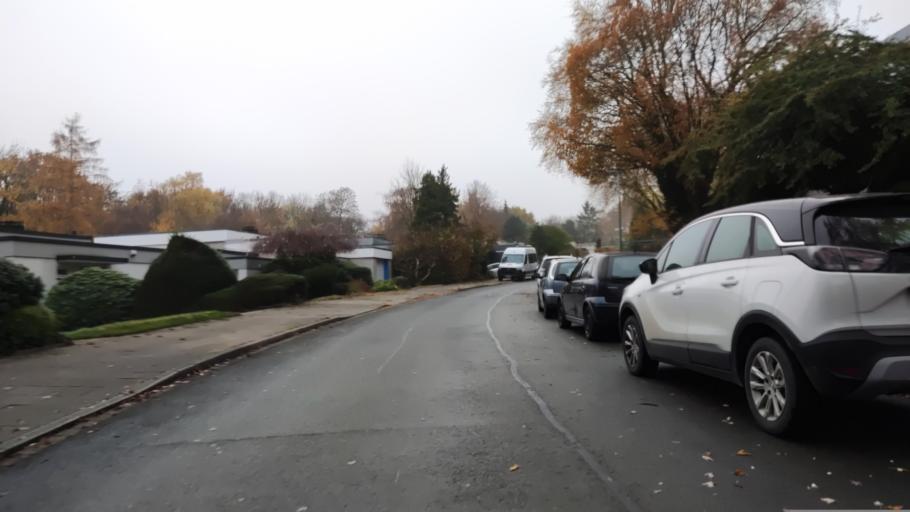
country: DE
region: North Rhine-Westphalia
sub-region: Regierungsbezirk Arnsberg
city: Bochum
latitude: 51.4552
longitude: 7.2527
